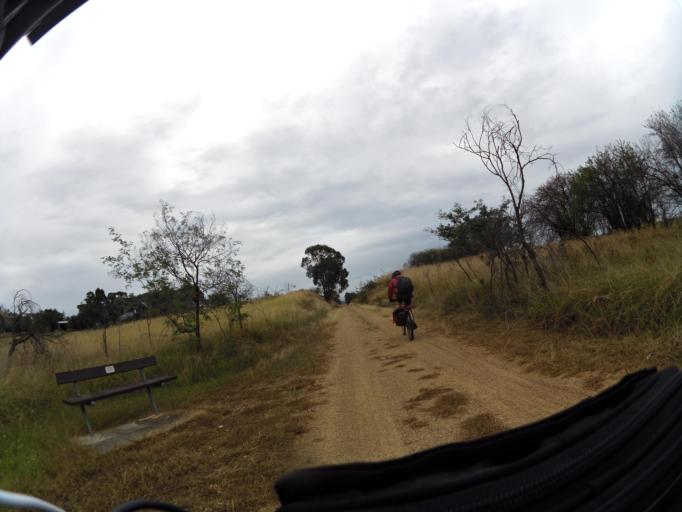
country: AU
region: New South Wales
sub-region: Albury Municipality
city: East Albury
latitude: -36.2121
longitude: 147.0555
